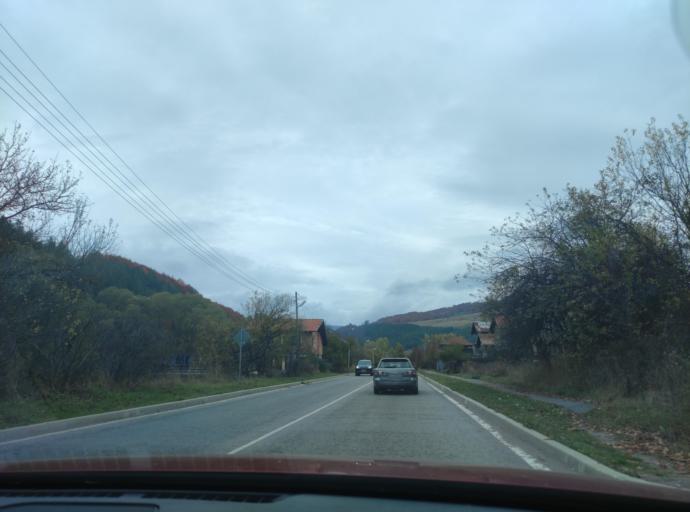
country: BG
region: Sofiya
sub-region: Obshtina Godech
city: Godech
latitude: 43.0743
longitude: 23.1080
